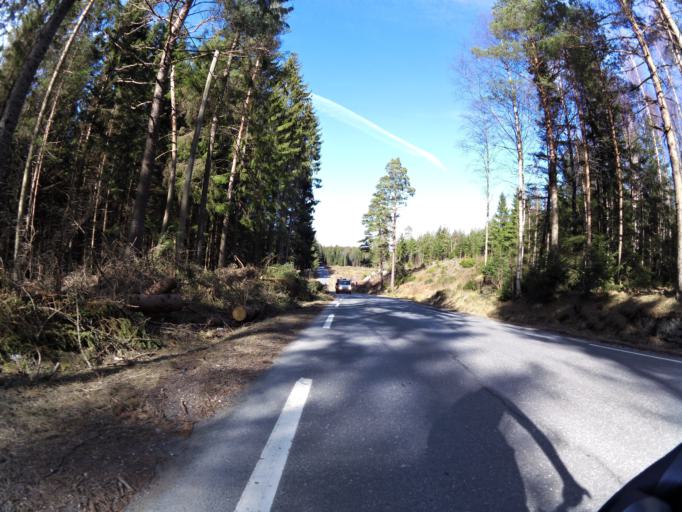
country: NO
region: Ostfold
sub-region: Fredrikstad
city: Fredrikstad
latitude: 59.2692
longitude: 10.9402
